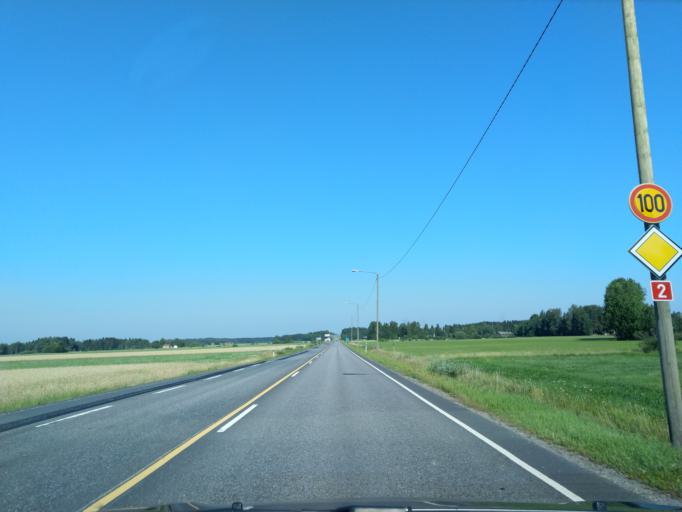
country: FI
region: Pirkanmaa
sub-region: Lounais-Pirkanmaa
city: Punkalaidun
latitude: 61.0408
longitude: 22.9942
